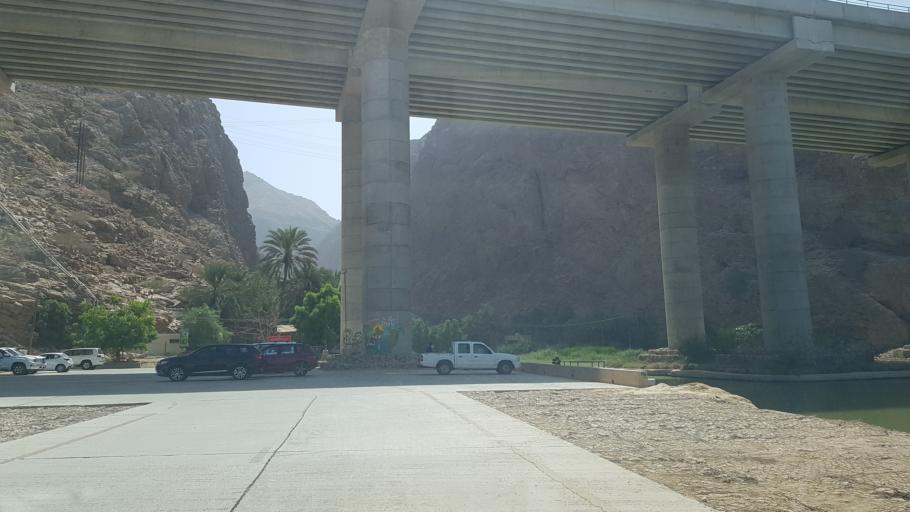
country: OM
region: Ash Sharqiyah
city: Sur
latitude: 22.8393
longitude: 59.2463
